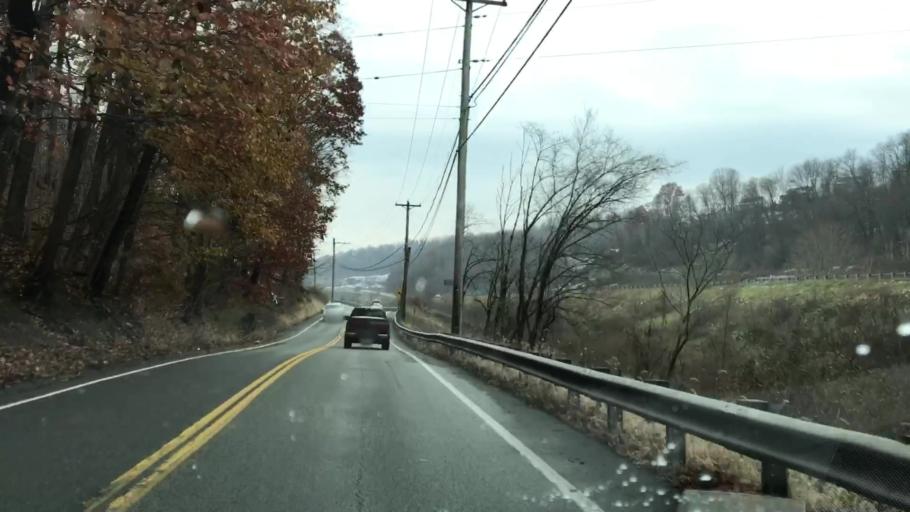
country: US
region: Pennsylvania
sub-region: Allegheny County
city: Franklin Park
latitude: 40.5468
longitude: -80.0834
